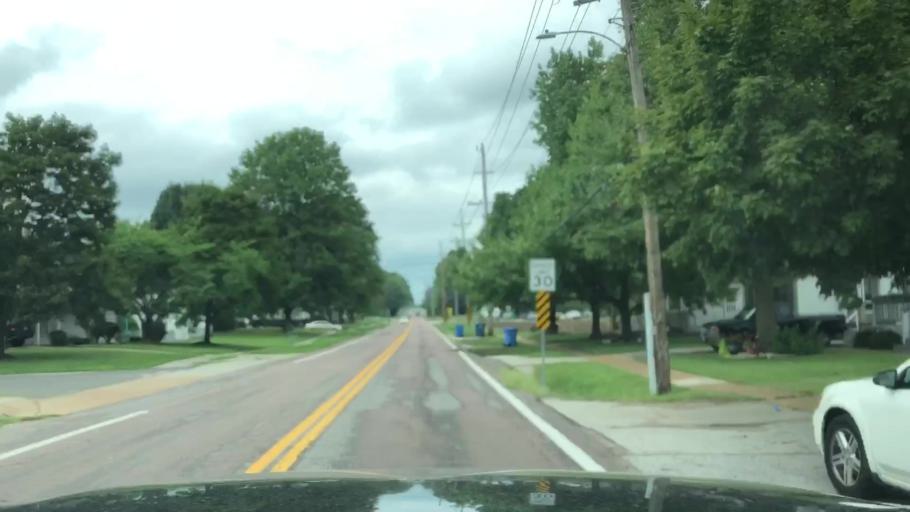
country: US
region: Missouri
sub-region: Saint Louis County
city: Florissant
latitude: 38.8029
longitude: -90.3488
